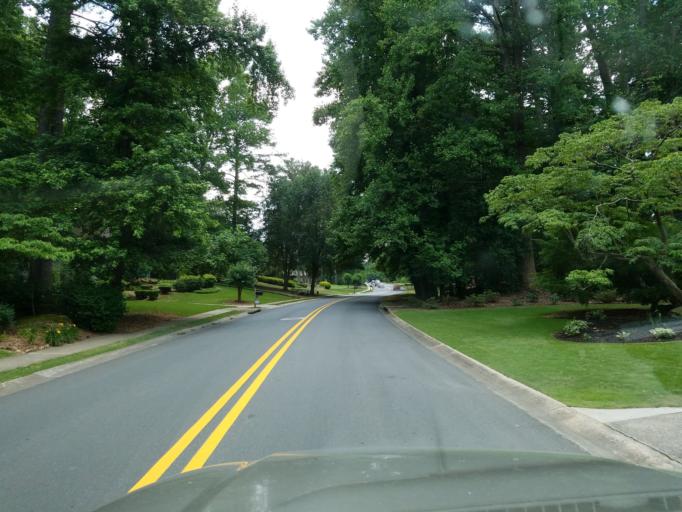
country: US
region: Georgia
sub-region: Fulton County
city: Sandy Springs
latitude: 33.9679
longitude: -84.4255
